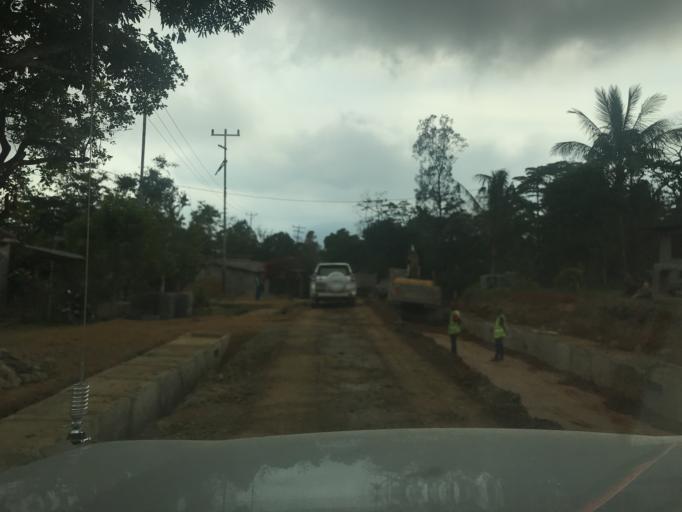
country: TL
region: Ainaro
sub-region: Ainaro
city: Ainaro
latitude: -8.9991
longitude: 125.5024
